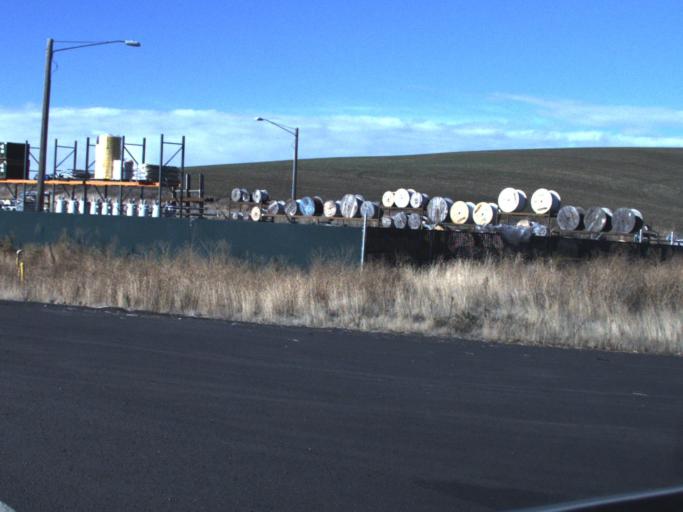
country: US
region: Washington
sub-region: Whitman County
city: Pullman
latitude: 46.7277
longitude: -117.1166
